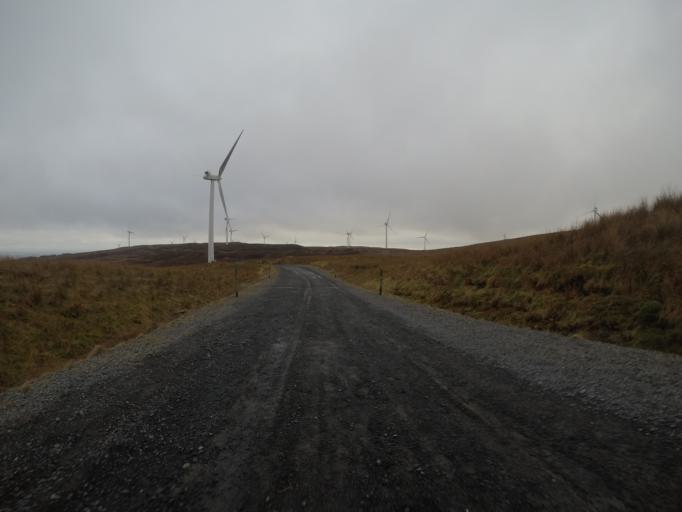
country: GB
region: Scotland
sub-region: North Ayrshire
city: Fairlie
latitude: 55.7569
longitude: -4.7954
